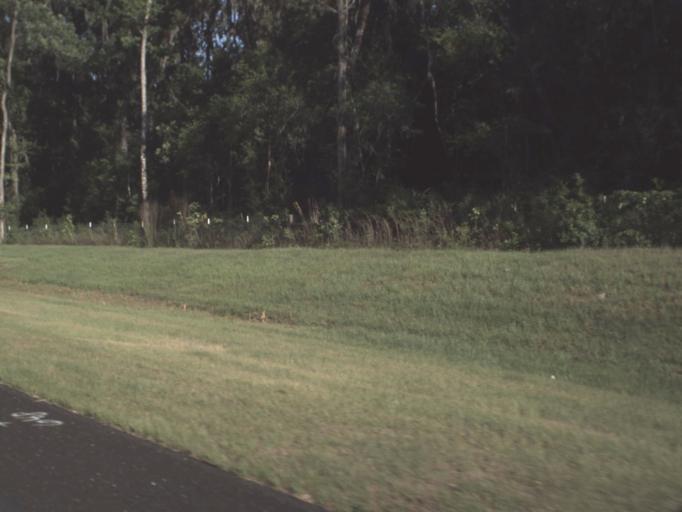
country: US
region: Florida
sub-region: Marion County
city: Ocala
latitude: 29.1867
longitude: -82.2791
